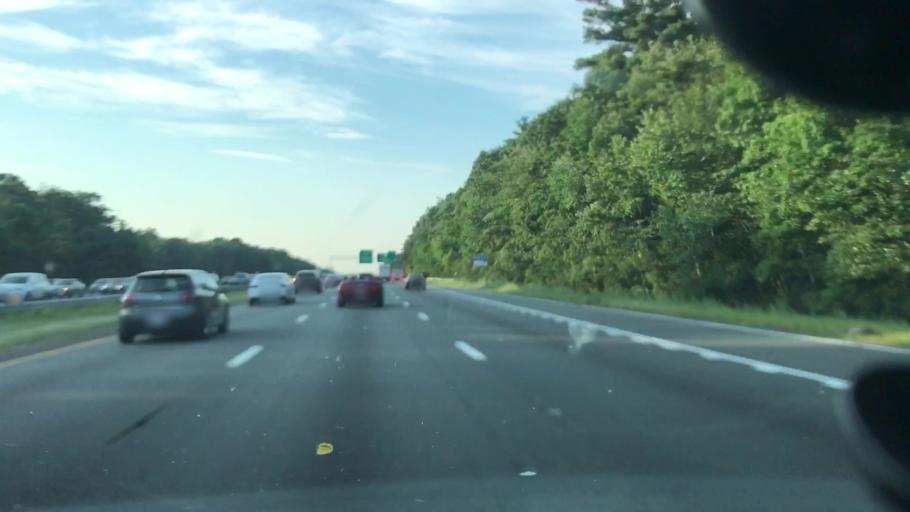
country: US
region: Massachusetts
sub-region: Essex County
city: Andover
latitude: 42.6393
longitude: -71.1825
